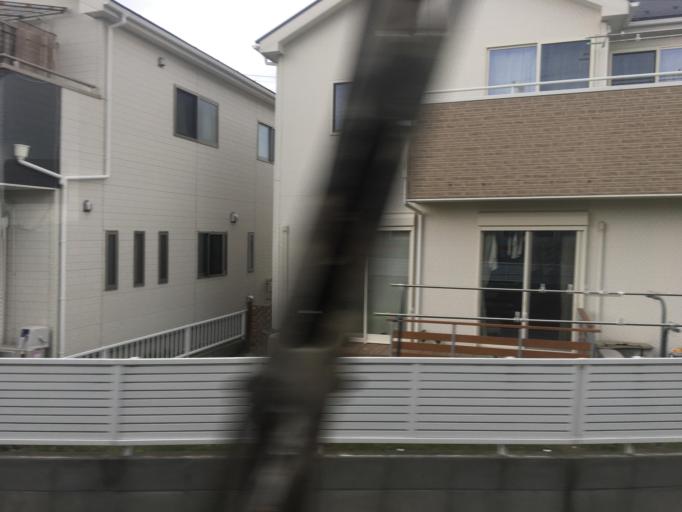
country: JP
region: Gunma
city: Maebashi-shi
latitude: 36.3890
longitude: 139.0784
